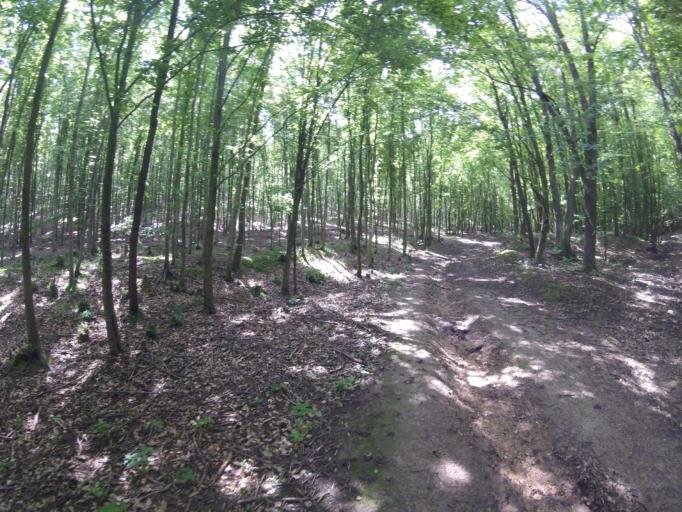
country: HU
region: Veszprem
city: Urkut
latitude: 47.1080
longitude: 17.6530
